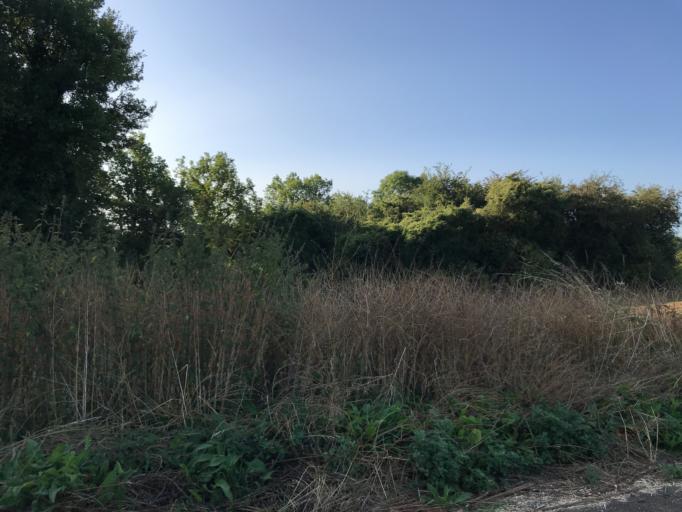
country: LU
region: Luxembourg
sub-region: Canton d'Esch-sur-Alzette
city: Niedercorn
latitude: 49.5349
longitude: 5.8780
